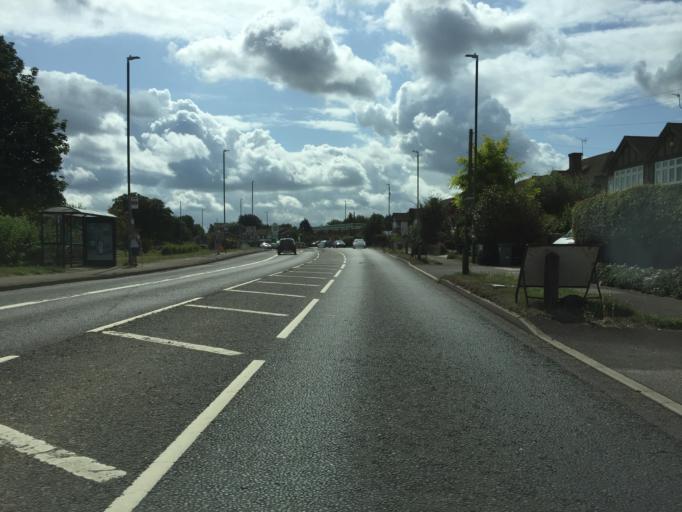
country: GB
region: England
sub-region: Kent
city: Aylesford
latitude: 51.2861
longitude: 0.4932
